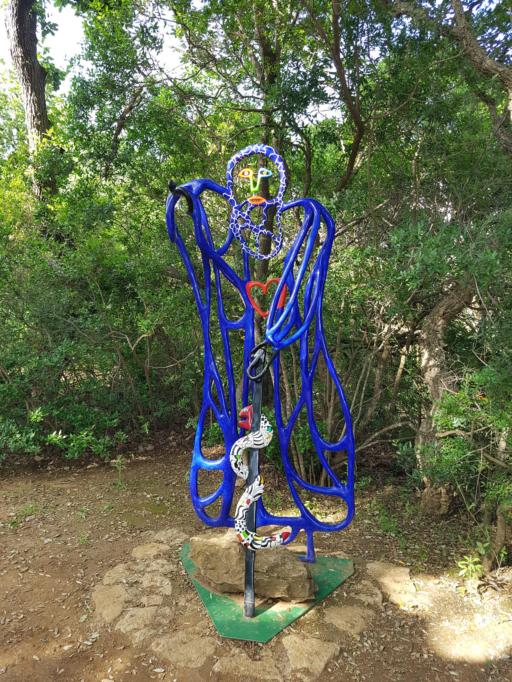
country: IT
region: Latium
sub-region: Provincia di Viterbo
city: Pescia Romana
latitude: 42.3869
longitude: 11.4536
